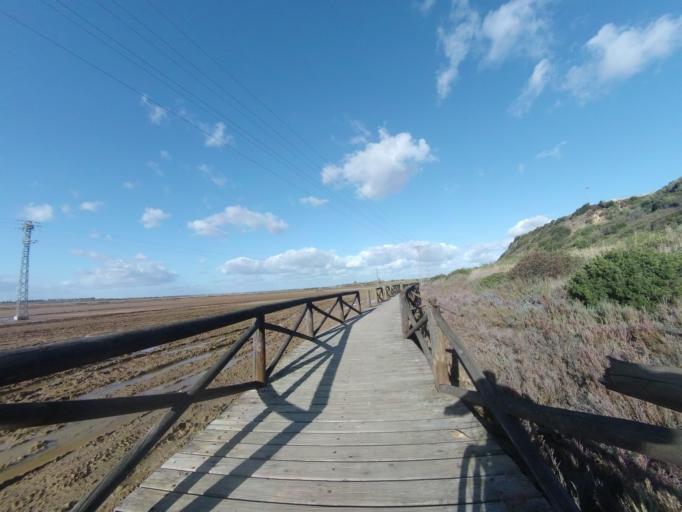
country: ES
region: Andalusia
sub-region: Provincia de Huelva
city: Palos de la Frontera
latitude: 37.2517
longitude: -6.8788
